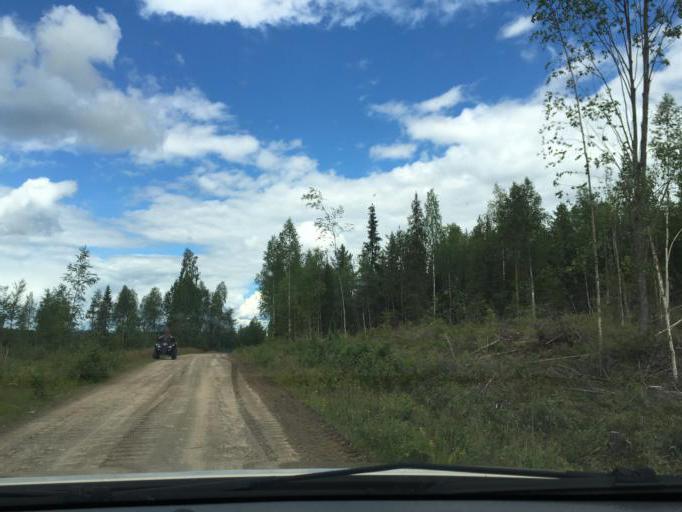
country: SE
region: Norrbotten
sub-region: Overkalix Kommun
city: OEverkalix
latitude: 66.1406
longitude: 22.7854
